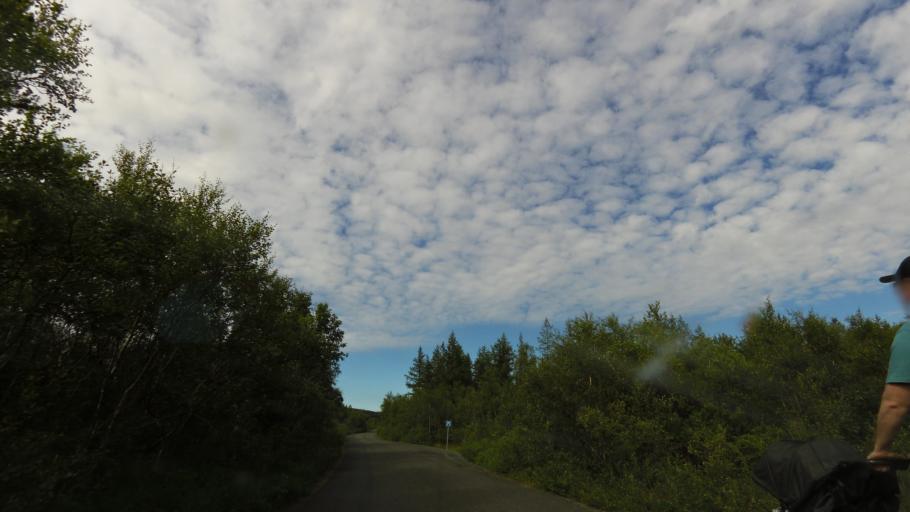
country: IS
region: Northeast
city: Husavik
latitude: 66.0032
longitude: -16.5095
